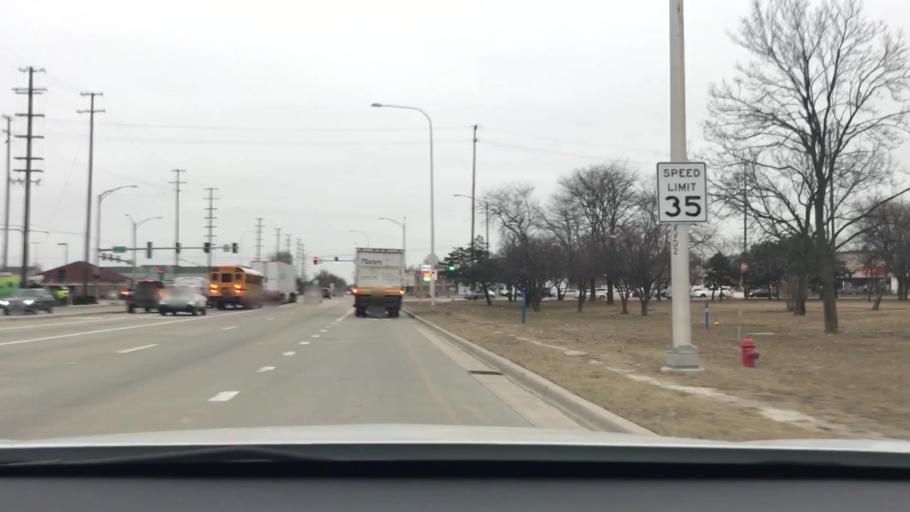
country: US
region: Illinois
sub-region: Cook County
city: Elk Grove Village
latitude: 42.0215
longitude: -87.9403
